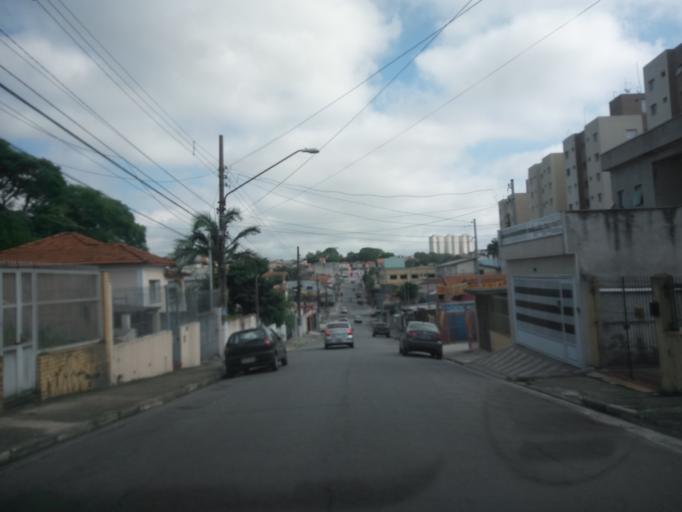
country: BR
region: Sao Paulo
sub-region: Sao Bernardo Do Campo
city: Sao Bernardo do Campo
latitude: -23.7206
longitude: -46.5676
